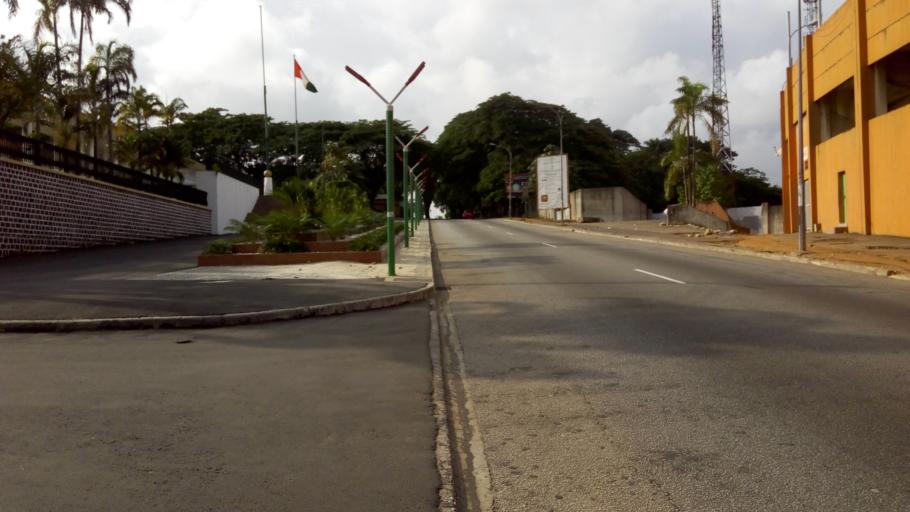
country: CI
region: Lagunes
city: Abidjan
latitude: 5.3285
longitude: -4.0196
